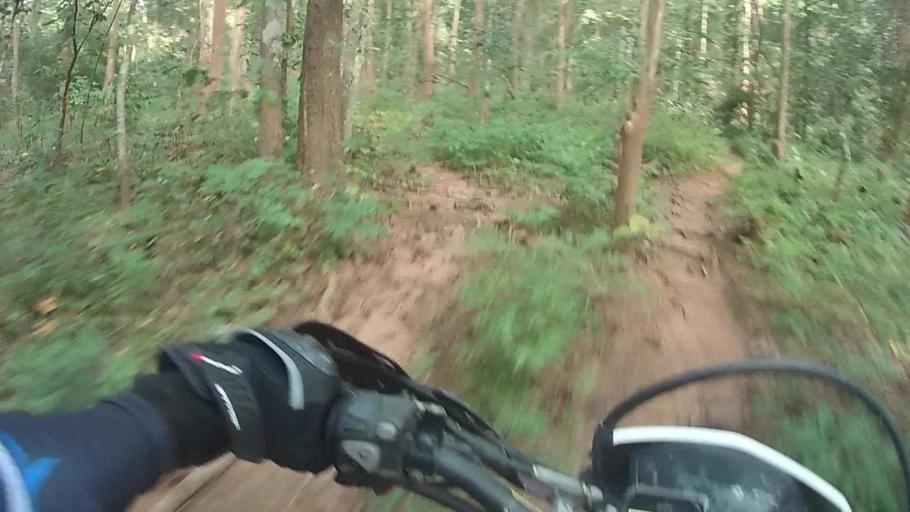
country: TH
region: Chiang Mai
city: San Sai
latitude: 18.9612
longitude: 99.0548
